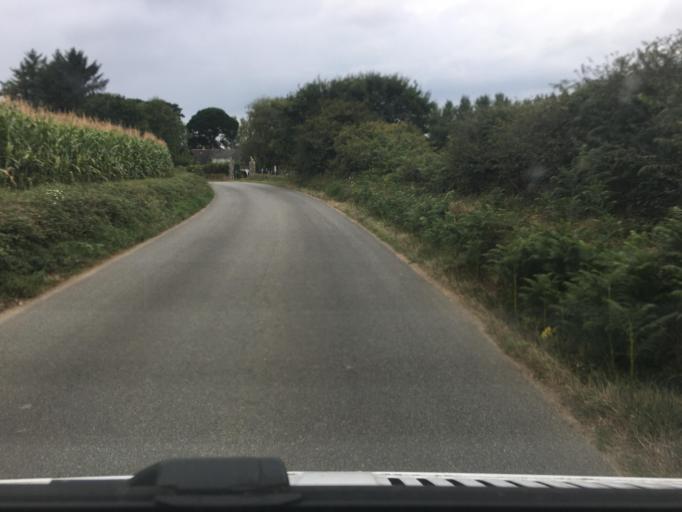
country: FR
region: Brittany
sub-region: Departement du Finistere
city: Beuzec-Cap-Sizun
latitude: 48.0775
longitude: -4.4760
